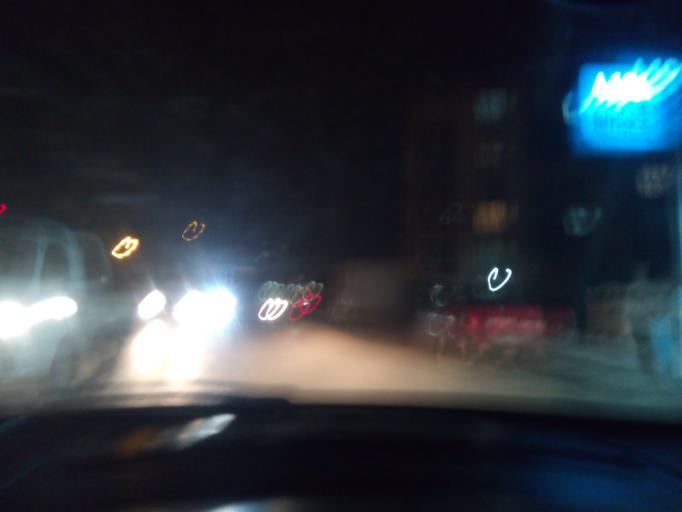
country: TR
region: Bursa
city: Niluefer
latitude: 40.2656
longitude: 28.9551
